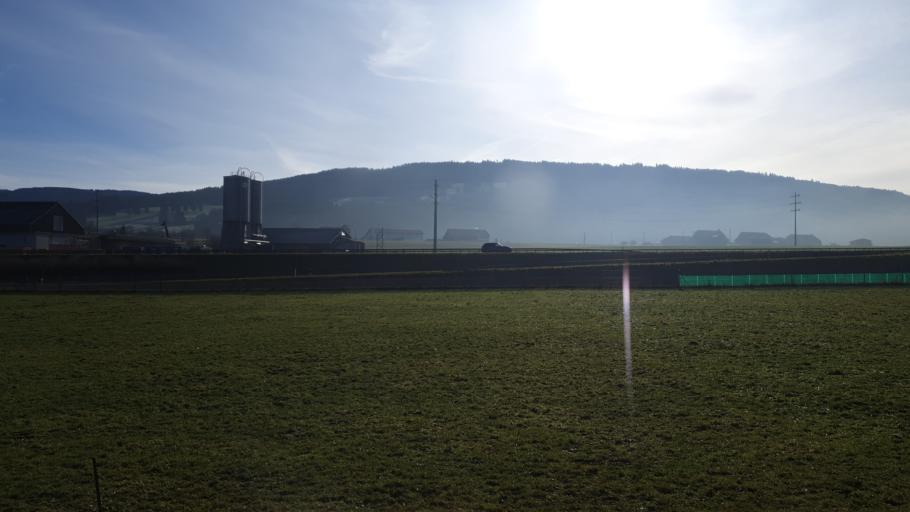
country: CH
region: Fribourg
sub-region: Gruyere District
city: Sales
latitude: 46.6159
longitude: 6.9718
